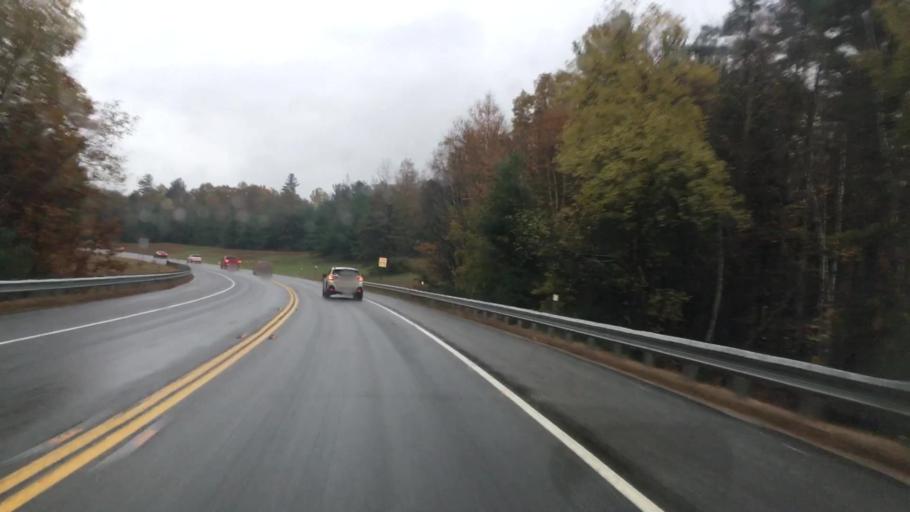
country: US
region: New Hampshire
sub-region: Hillsborough County
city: Wilton
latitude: 42.8370
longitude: -71.7012
